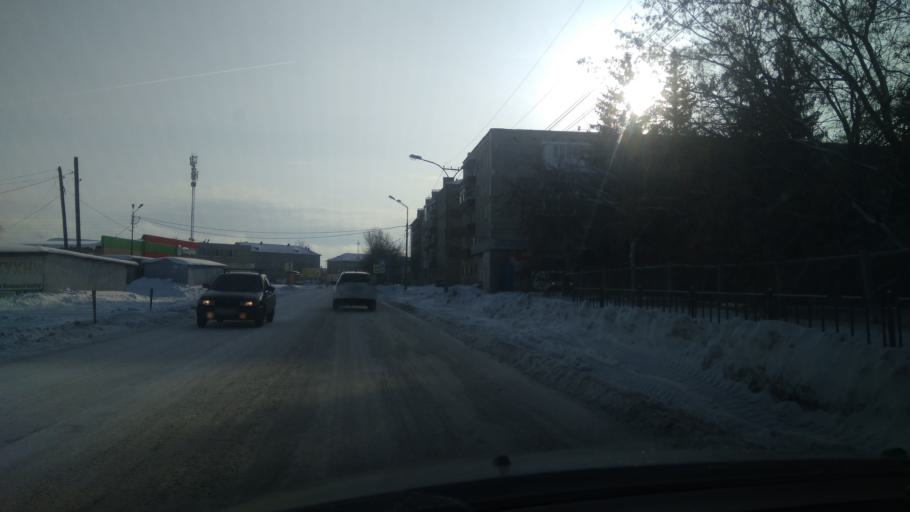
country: RU
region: Sverdlovsk
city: Sukhoy Log
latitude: 56.9108
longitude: 62.0322
